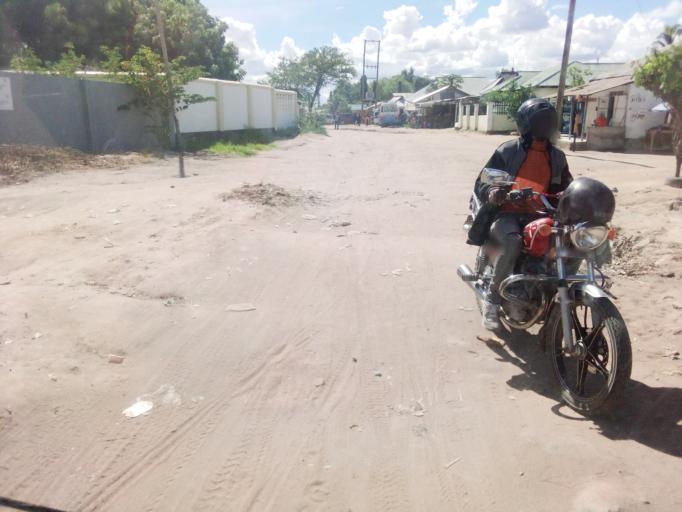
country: TZ
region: Dodoma
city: Dodoma
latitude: -6.1772
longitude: 35.7553
